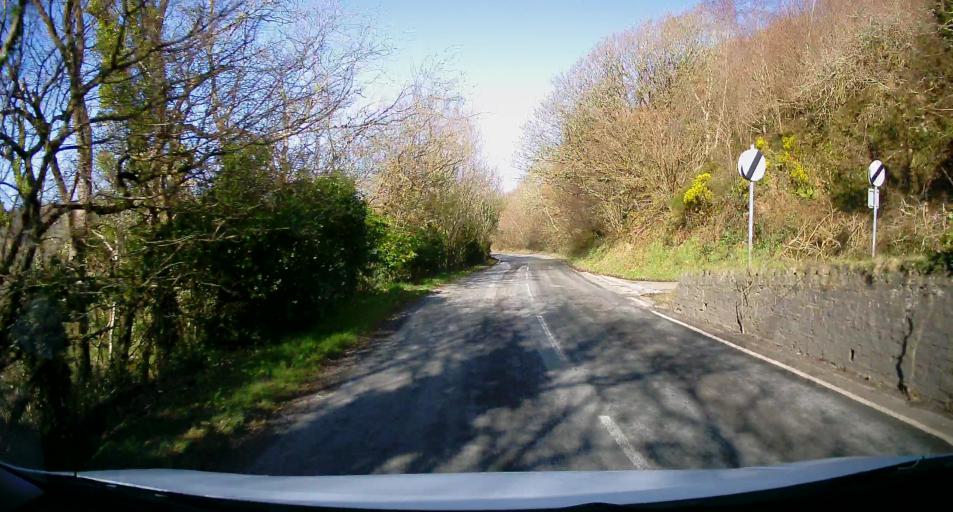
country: GB
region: Wales
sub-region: County of Ceredigion
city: Llanarth
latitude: 52.1956
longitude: -4.3150
